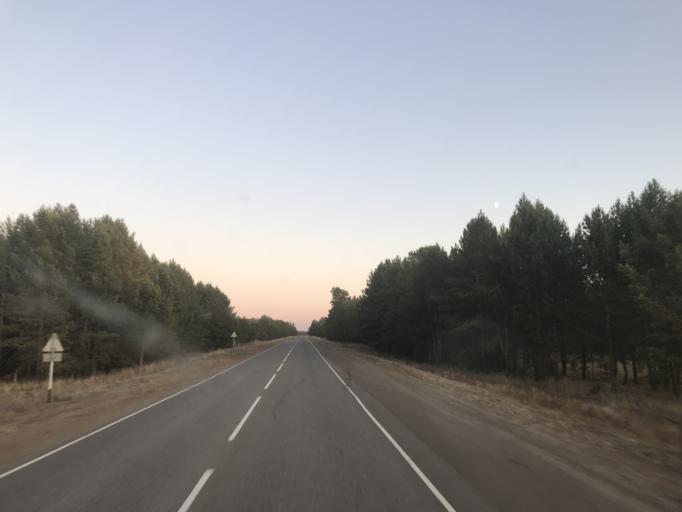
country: KZ
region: East Kazakhstan
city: Semey
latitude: 50.6491
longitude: 79.8942
